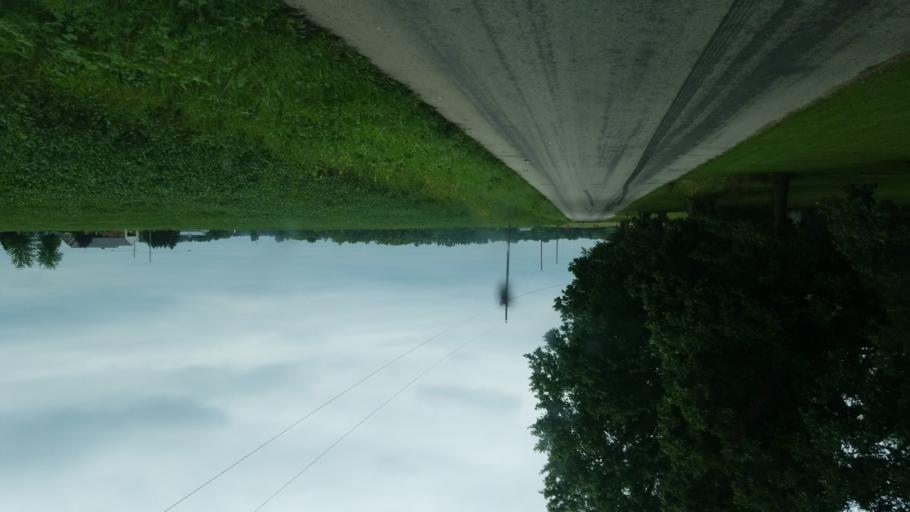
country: US
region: Ohio
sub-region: Morrow County
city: Mount Gilead
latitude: 40.5347
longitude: -82.8018
